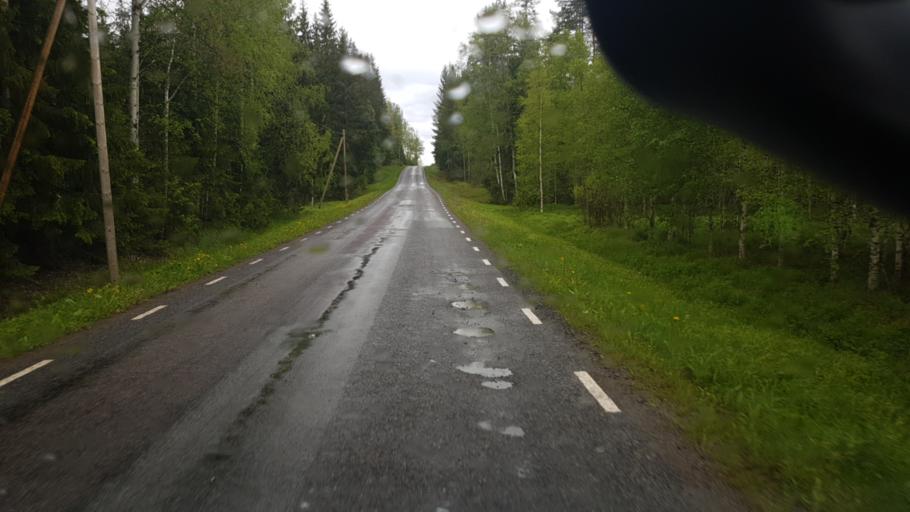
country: SE
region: Vaermland
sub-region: Eda Kommun
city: Amotfors
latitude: 59.8592
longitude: 12.4249
